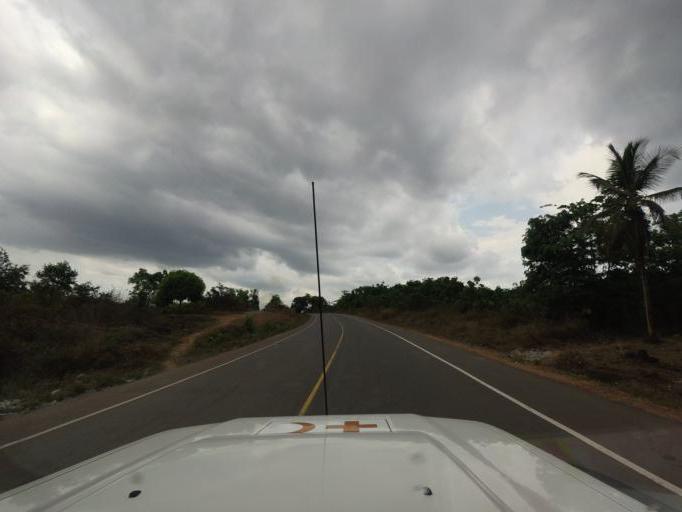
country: LR
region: Margibi
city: Kakata
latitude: 6.6668
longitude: -10.2291
